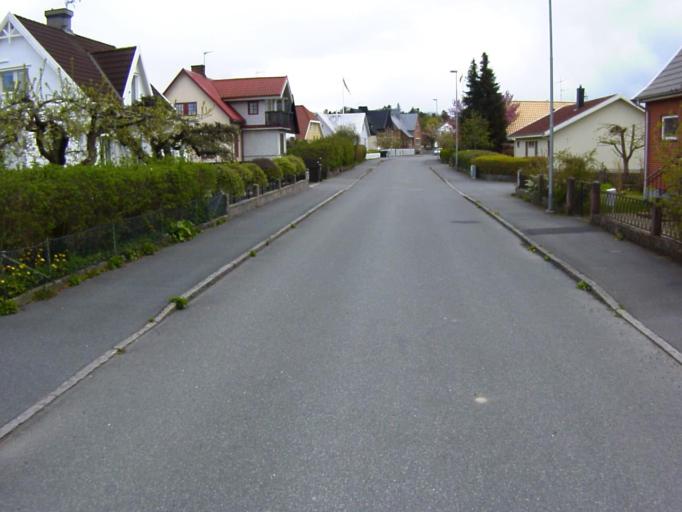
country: SE
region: Skane
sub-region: Kristianstads Kommun
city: Kristianstad
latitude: 56.0376
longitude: 14.1700
